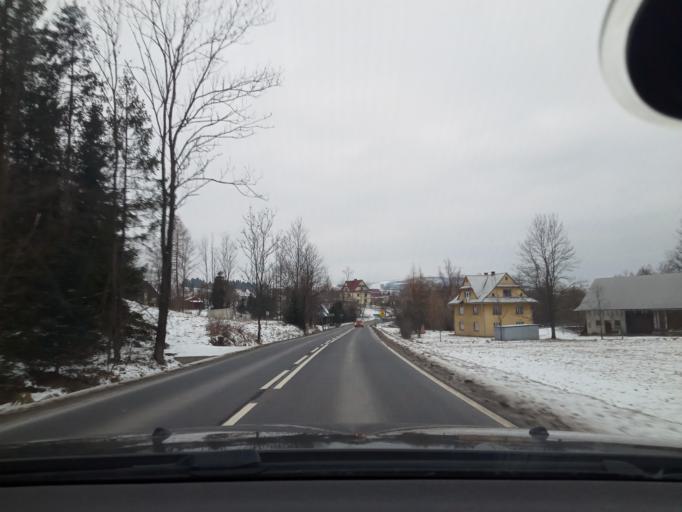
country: PL
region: Lesser Poland Voivodeship
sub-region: Powiat limanowski
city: Lubomierz
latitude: 49.6194
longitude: 20.1575
